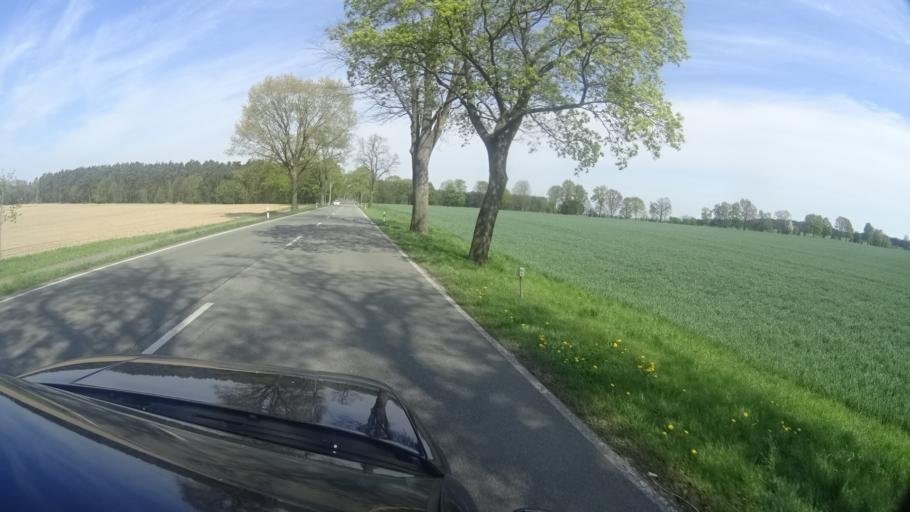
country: DE
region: Brandenburg
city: Friesack
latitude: 52.7136
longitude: 12.5933
